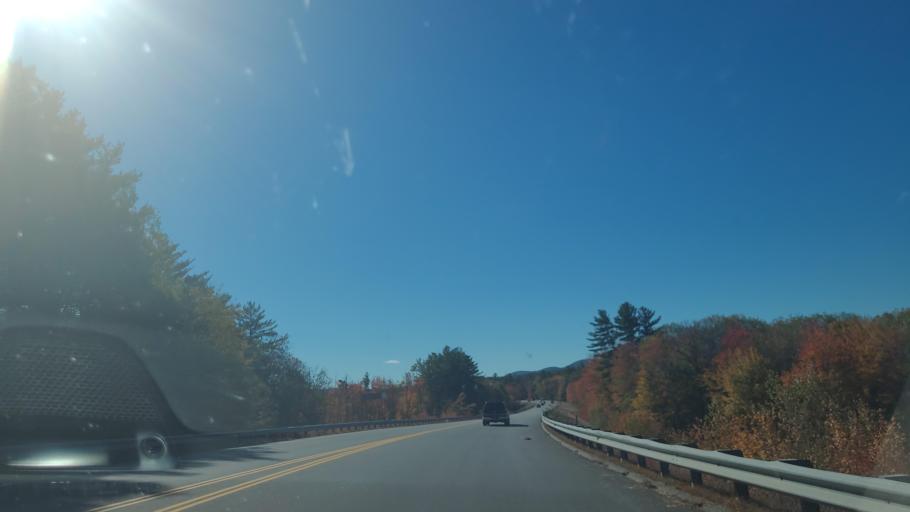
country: US
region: New Hampshire
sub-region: Carroll County
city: Conway
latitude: 44.0036
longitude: -71.0881
